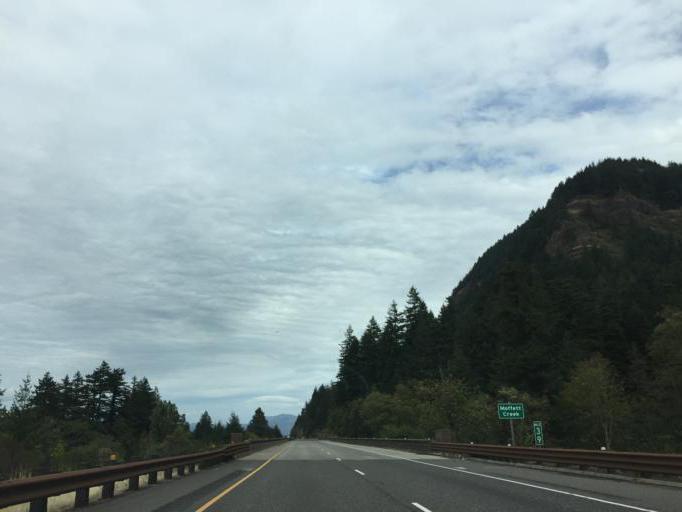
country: US
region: Oregon
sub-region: Hood River County
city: Cascade Locks
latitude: 45.6227
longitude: -121.9784
